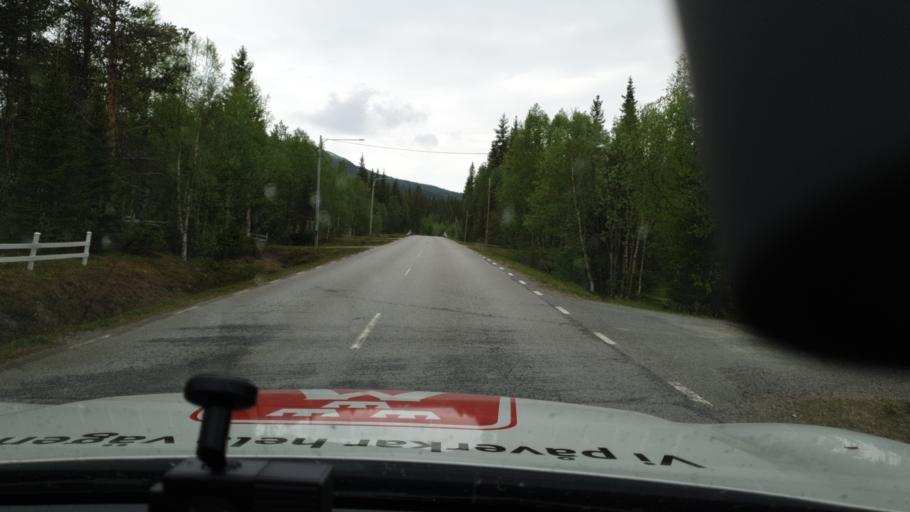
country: SE
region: Vaesterbotten
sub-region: Storumans Kommun
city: Fristad
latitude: 65.8845
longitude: 16.3781
